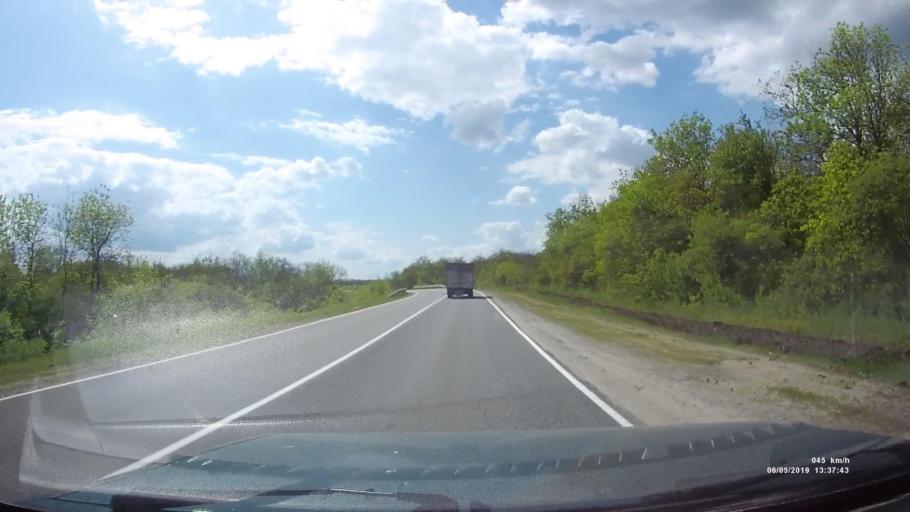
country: RU
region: Rostov
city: Ust'-Donetskiy
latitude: 47.6894
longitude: 40.7171
